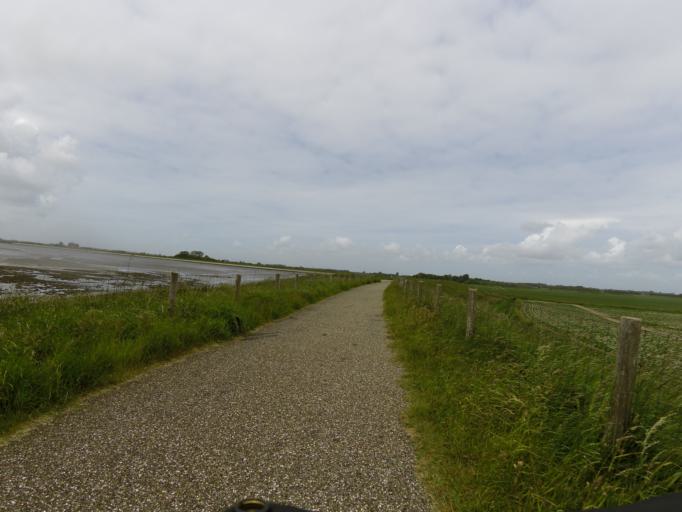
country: NL
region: Zeeland
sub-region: Schouwen-Duiveland
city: Bruinisse
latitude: 51.6289
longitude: 4.0551
